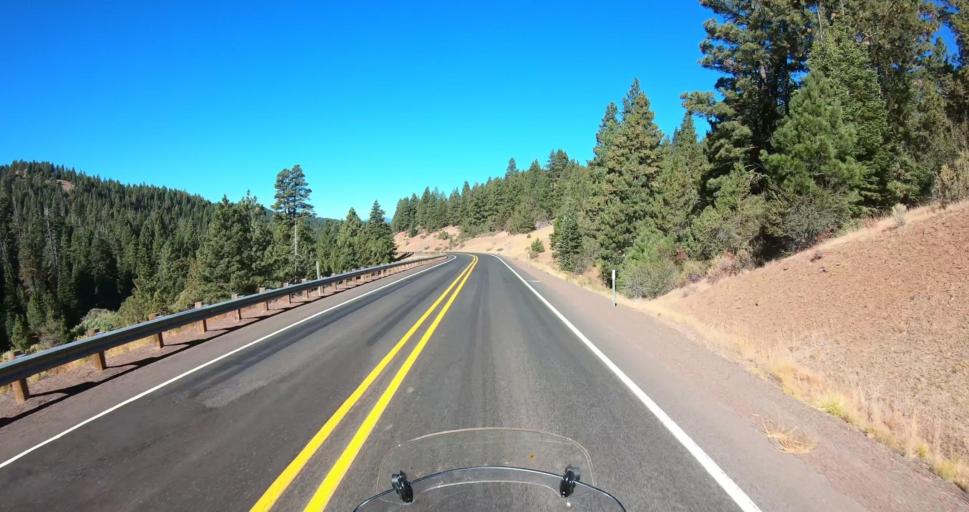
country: US
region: Oregon
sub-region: Lake County
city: Lakeview
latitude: 42.2388
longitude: -120.3022
